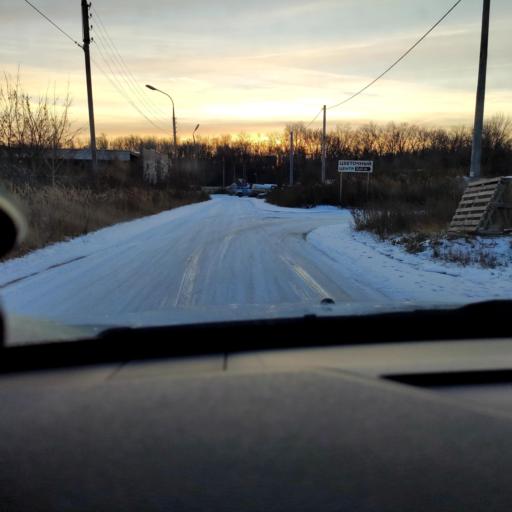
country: RU
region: Samara
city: Petra-Dubrava
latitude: 53.2638
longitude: 50.2848
